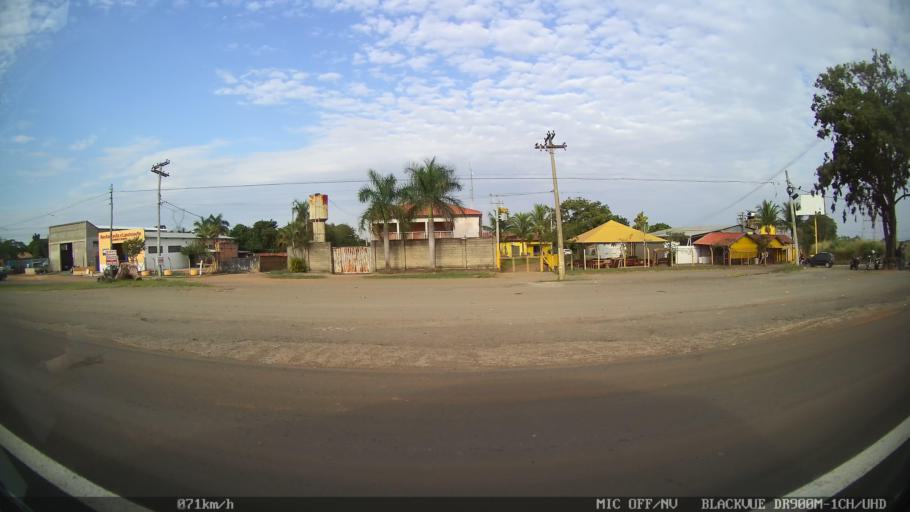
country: BR
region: Sao Paulo
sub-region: Artur Nogueira
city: Artur Nogueira
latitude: -22.6037
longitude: -47.1909
